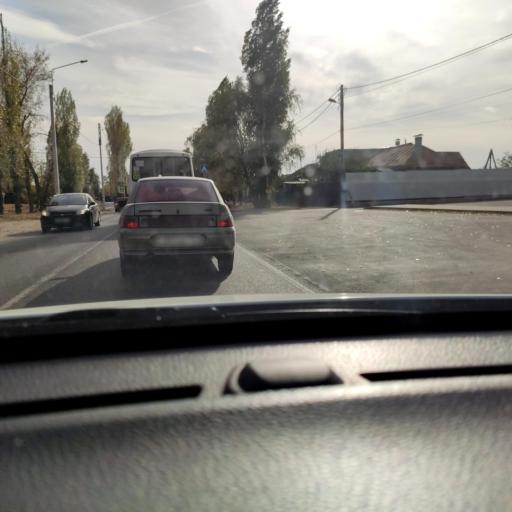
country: RU
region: Voronezj
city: Maslovka
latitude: 51.5526
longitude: 39.2359
